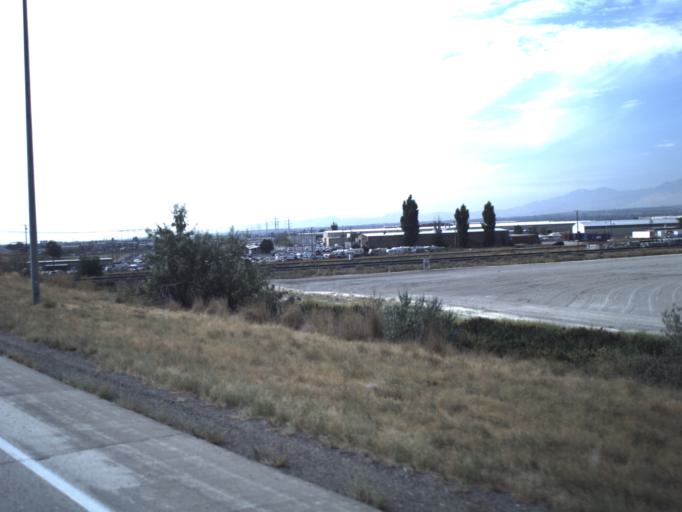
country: US
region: Utah
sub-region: Salt Lake County
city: Salt Lake City
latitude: 40.7616
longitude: -111.9528
